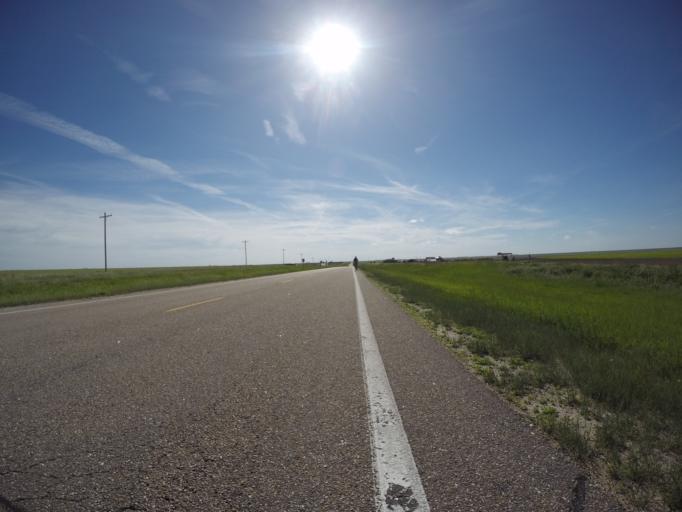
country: US
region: Kansas
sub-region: Cheyenne County
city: Saint Francis
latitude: 39.7566
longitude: -102.0077
